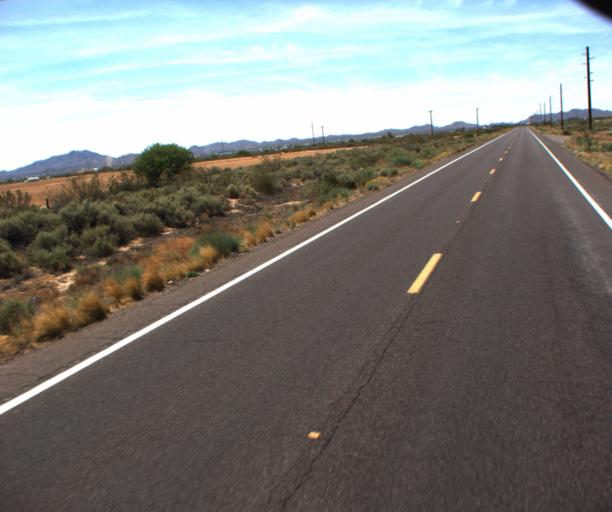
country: US
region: Arizona
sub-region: La Paz County
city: Salome
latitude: 33.7997
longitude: -113.5824
